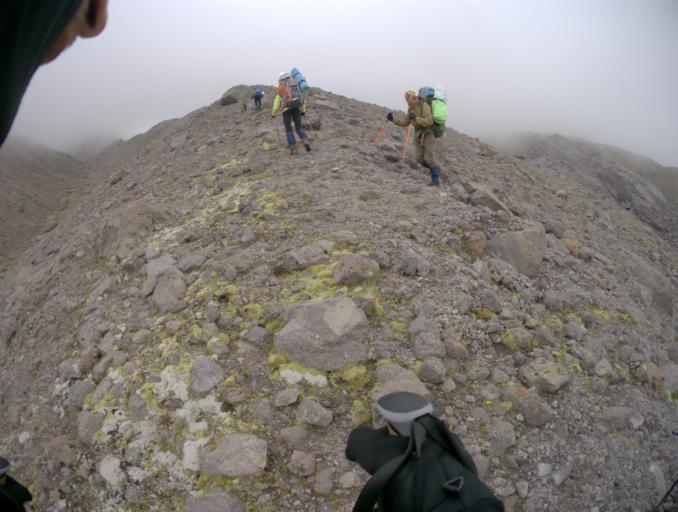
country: RU
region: Kabardino-Balkariya
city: Terskol
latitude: 43.3827
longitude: 42.3822
